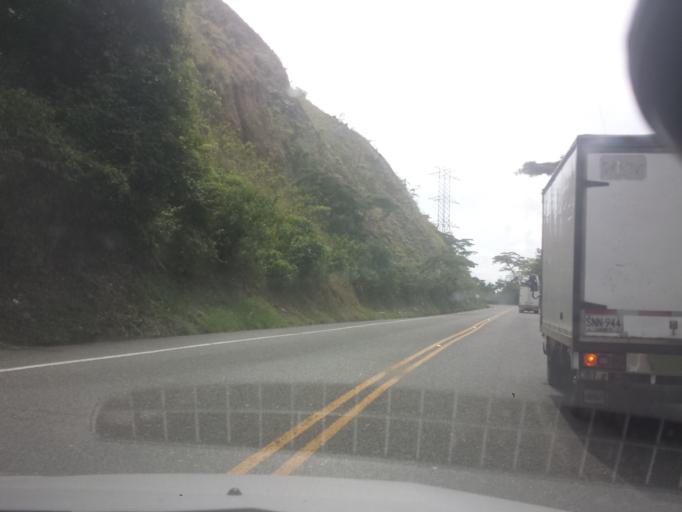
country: CO
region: Antioquia
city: Liborina
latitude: 6.6304
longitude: -75.8733
